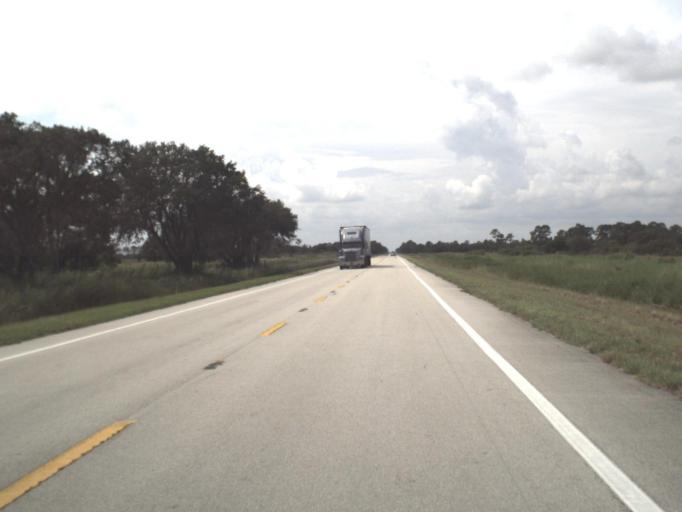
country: US
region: Florida
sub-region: Hendry County
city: Port LaBelle
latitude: 26.8497
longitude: -81.3807
